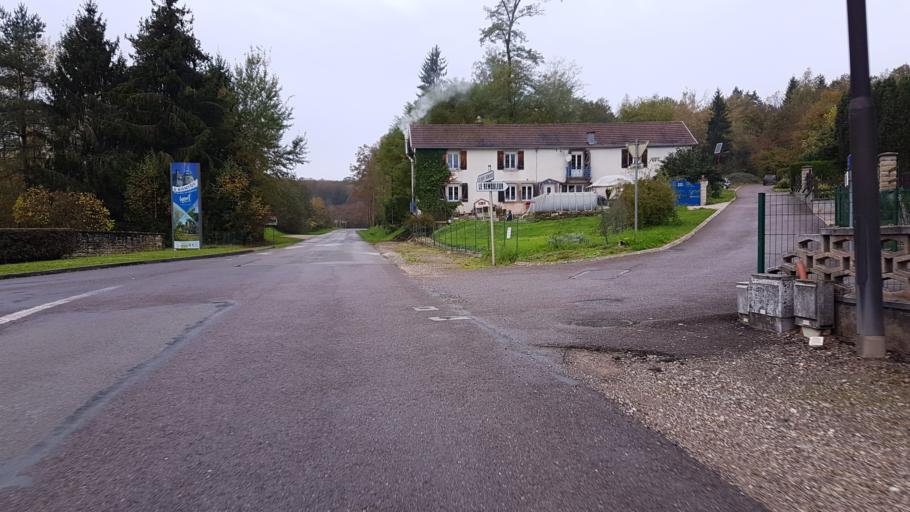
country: FR
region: Franche-Comte
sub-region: Departement de la Haute-Saone
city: Luxeuil-les-Bains
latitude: 47.8264
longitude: 6.3668
